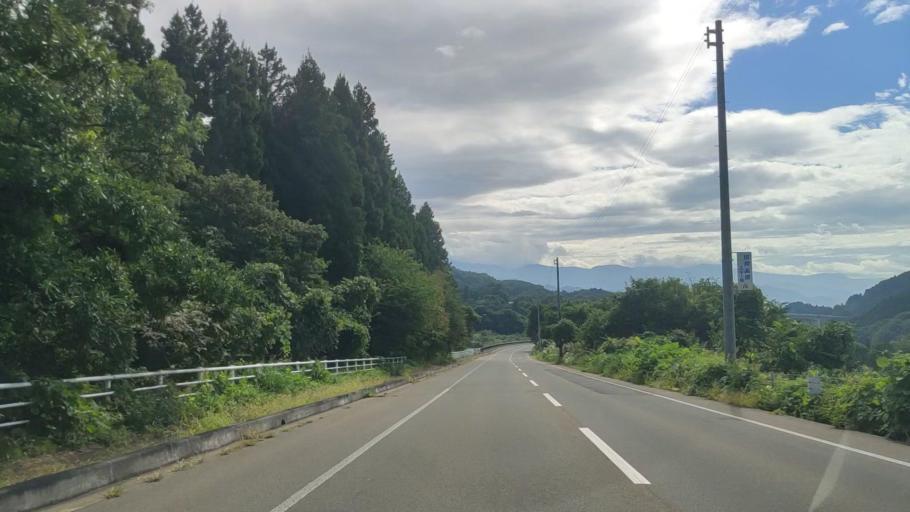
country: JP
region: Nagano
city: Nakano
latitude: 36.7924
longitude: 138.3161
